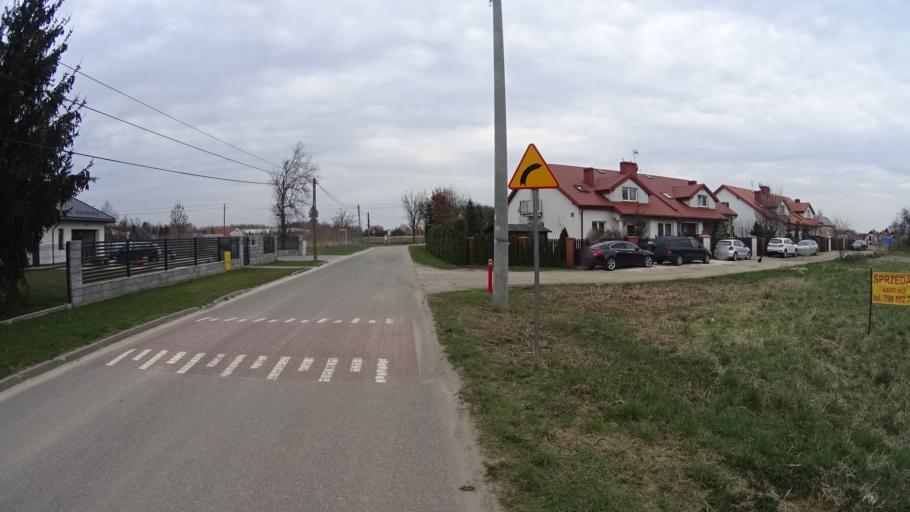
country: PL
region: Masovian Voivodeship
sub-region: Powiat warszawski zachodni
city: Jozefow
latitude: 52.2063
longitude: 20.6822
